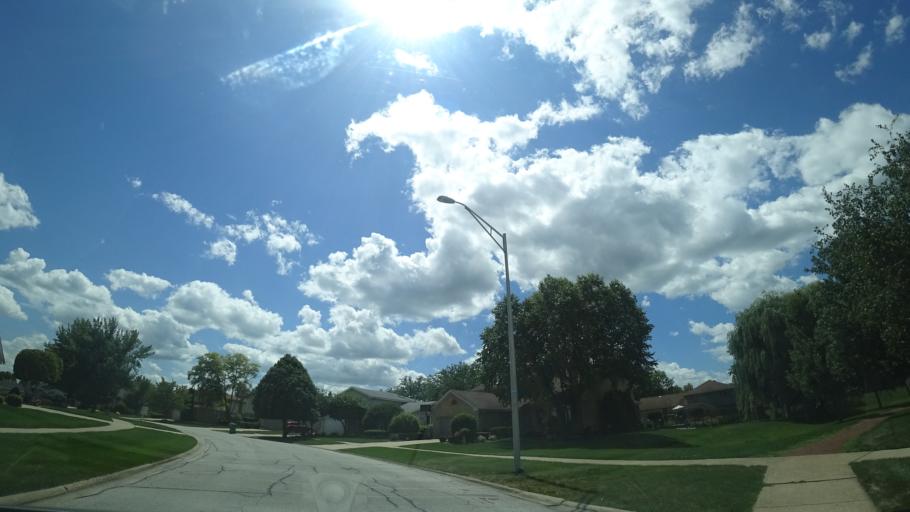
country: US
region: Illinois
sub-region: Will County
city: Homer Glen
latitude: 41.5755
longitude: -87.9057
